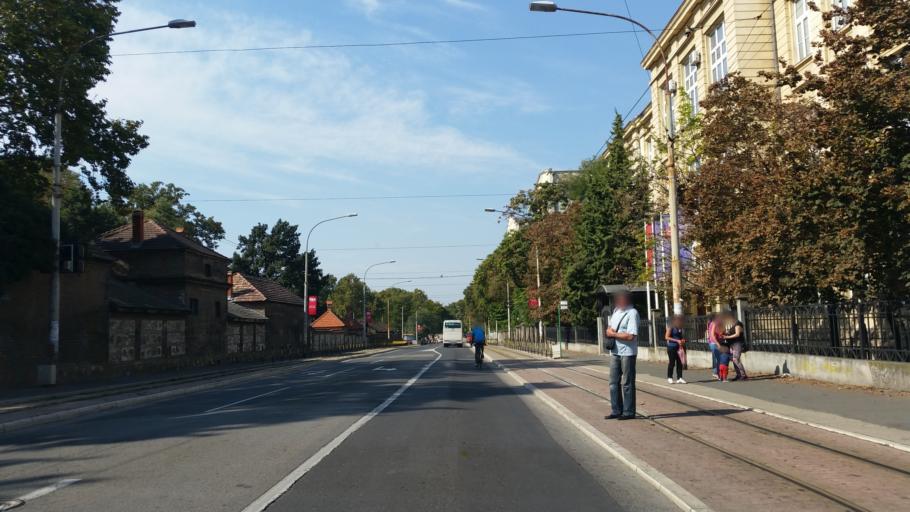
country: RS
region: Central Serbia
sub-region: Belgrade
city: Stari Grad
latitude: 44.8260
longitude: 20.4554
